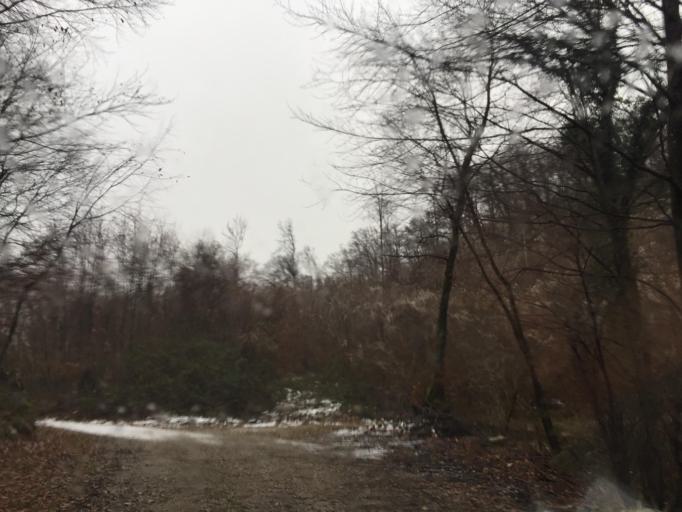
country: SI
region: Kanal
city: Kanal
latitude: 46.0692
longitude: 13.6708
